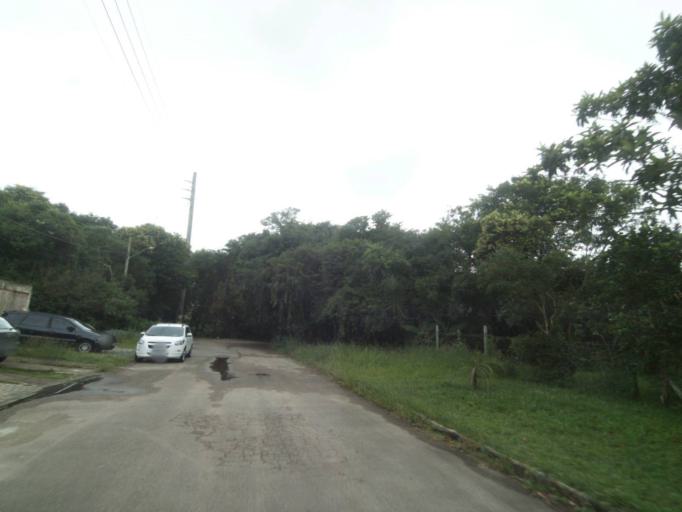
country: BR
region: Parana
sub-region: Curitiba
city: Curitiba
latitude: -25.4472
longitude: -49.3159
